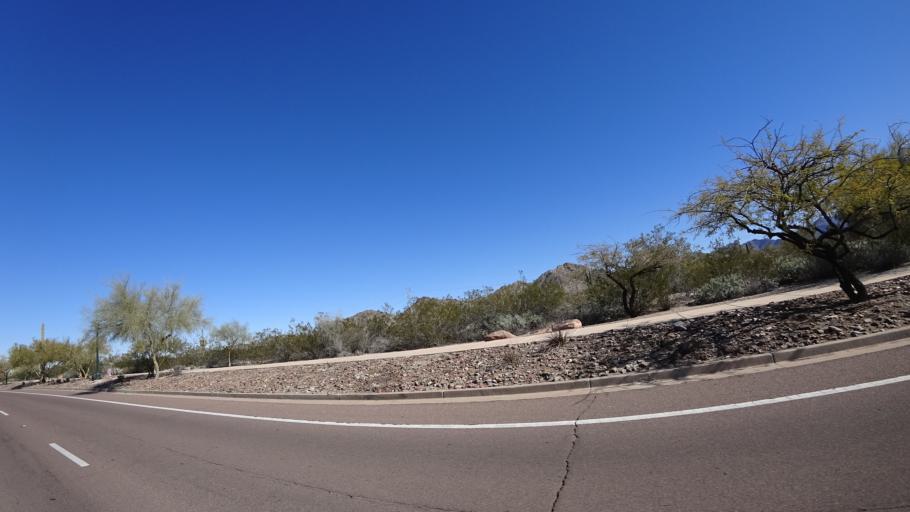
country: US
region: Arizona
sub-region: Maricopa County
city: Goodyear
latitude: 33.3388
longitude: -112.4235
